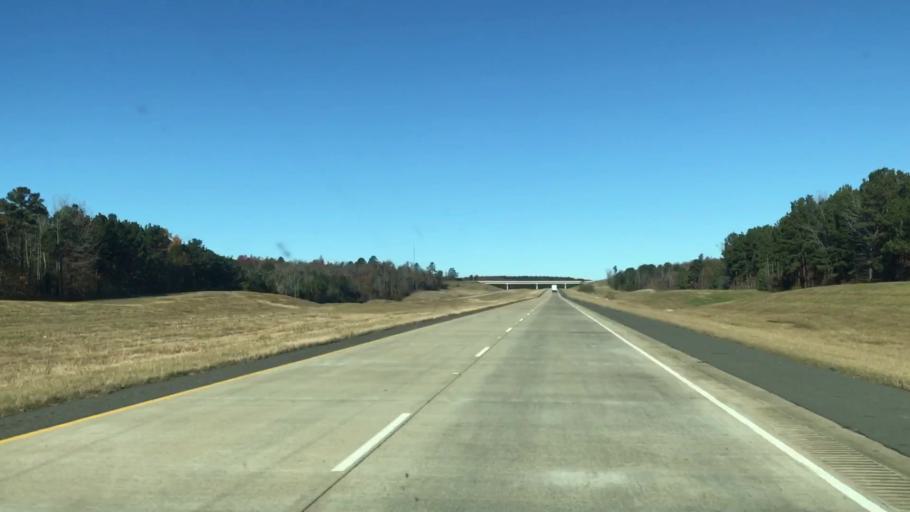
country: US
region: Louisiana
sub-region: Caddo Parish
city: Vivian
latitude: 32.9171
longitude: -93.8793
